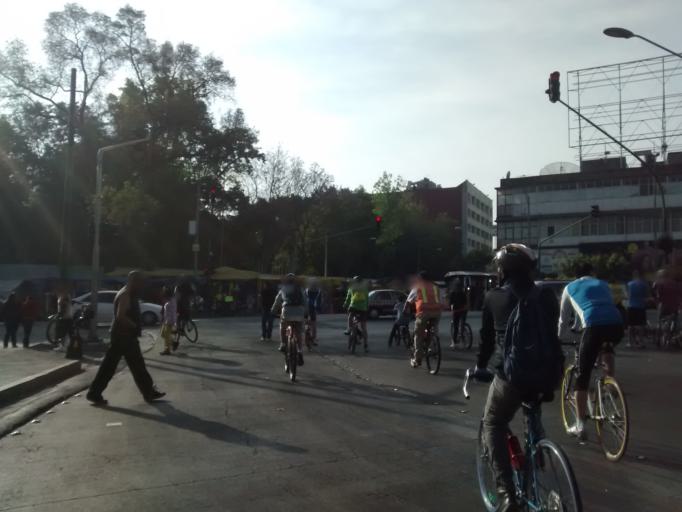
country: MX
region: Mexico City
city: Mexico City
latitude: 19.4263
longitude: -99.1309
